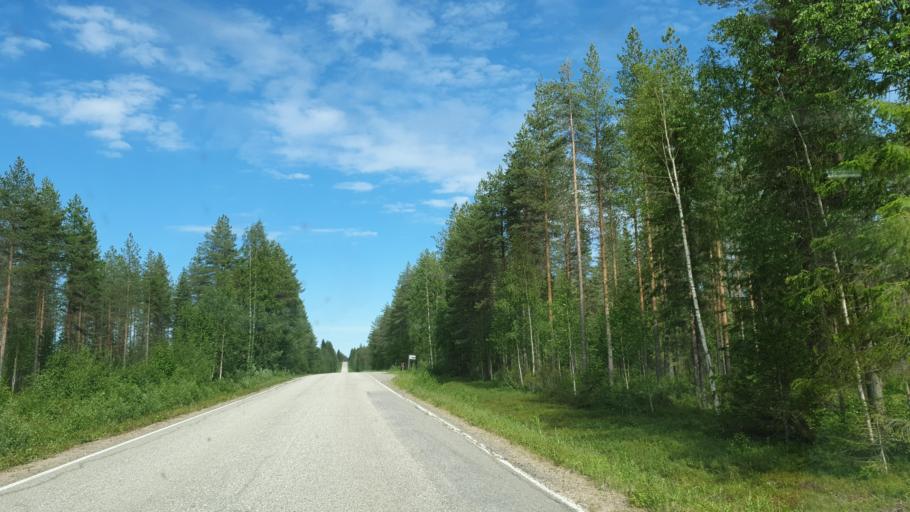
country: FI
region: Kainuu
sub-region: Kehys-Kainuu
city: Suomussalmi
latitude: 64.5801
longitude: 29.0412
